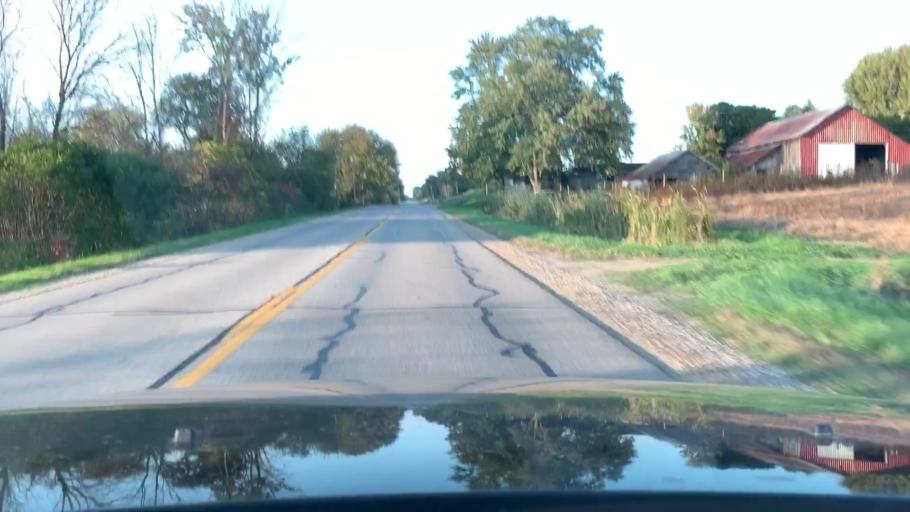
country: US
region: Michigan
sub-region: Ottawa County
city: Hudsonville
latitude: 42.7915
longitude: -85.8417
